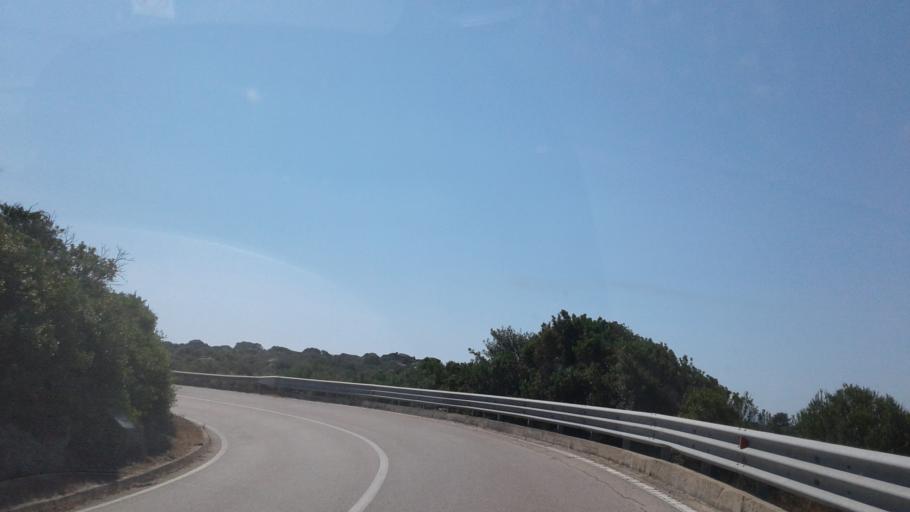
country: IT
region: Sardinia
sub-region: Provincia di Olbia-Tempio
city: Palau
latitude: 41.1285
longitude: 9.2897
